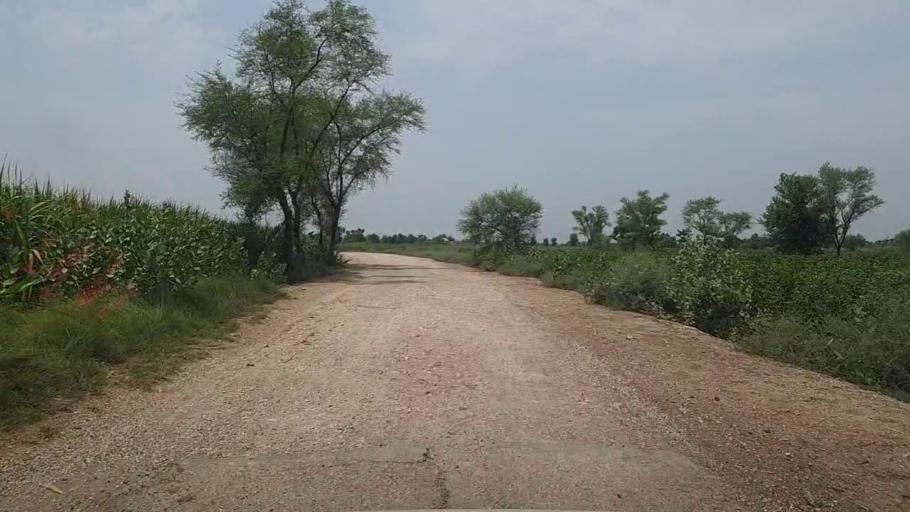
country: PK
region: Sindh
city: Karaundi
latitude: 26.9171
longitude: 68.3296
